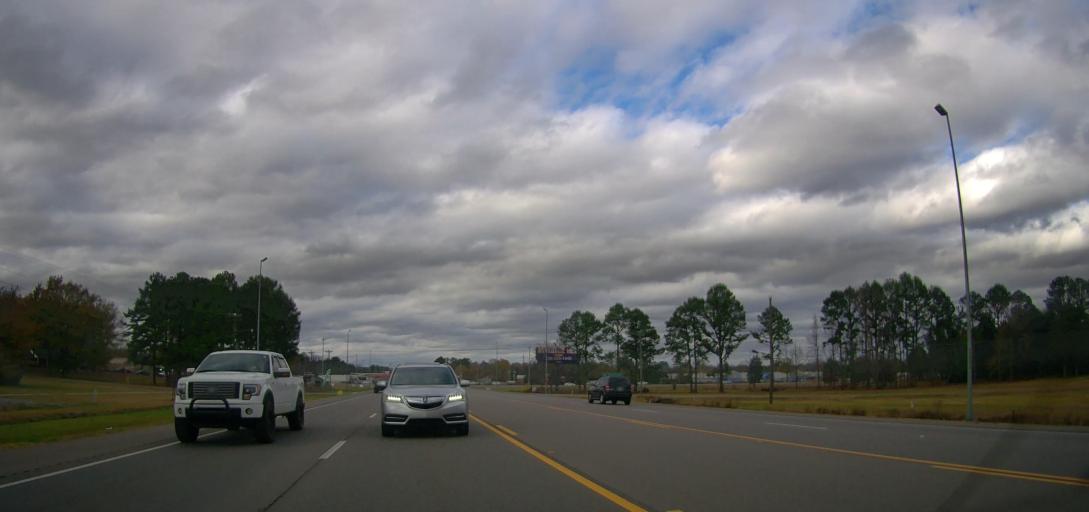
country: US
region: Alabama
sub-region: Lawrence County
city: Moulton
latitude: 34.4899
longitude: -87.2776
